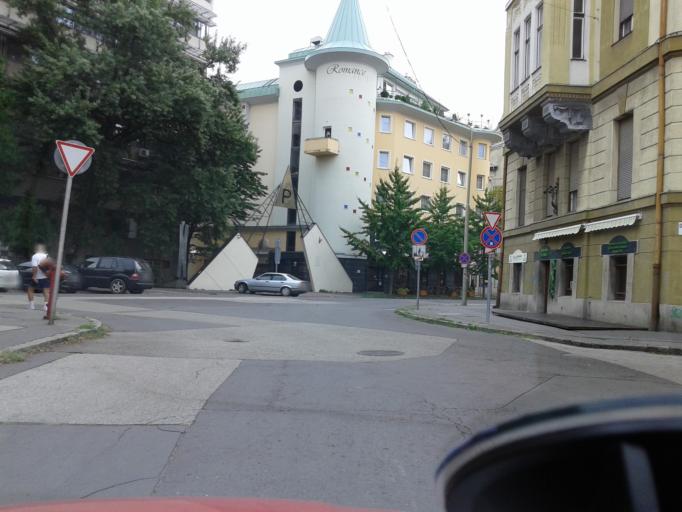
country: HU
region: Csongrad
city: Szeged
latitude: 46.2552
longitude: 20.1525
